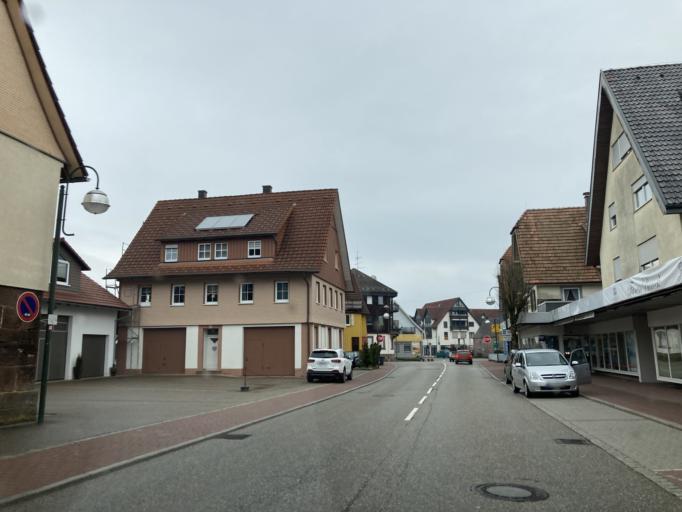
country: DE
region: Baden-Wuerttemberg
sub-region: Karlsruhe Region
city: Lossburg
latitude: 48.4102
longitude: 8.4533
